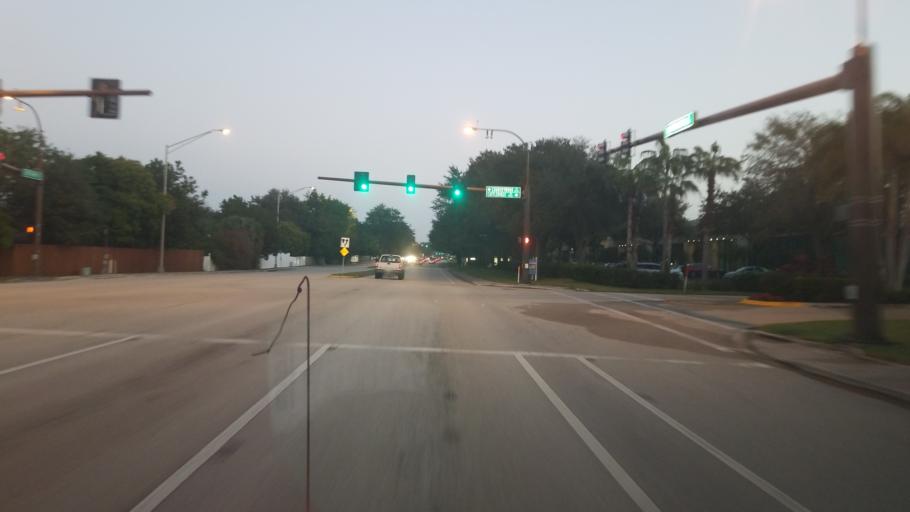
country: US
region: Florida
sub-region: Sarasota County
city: Lake Sarasota
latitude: 27.3055
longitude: -82.4514
